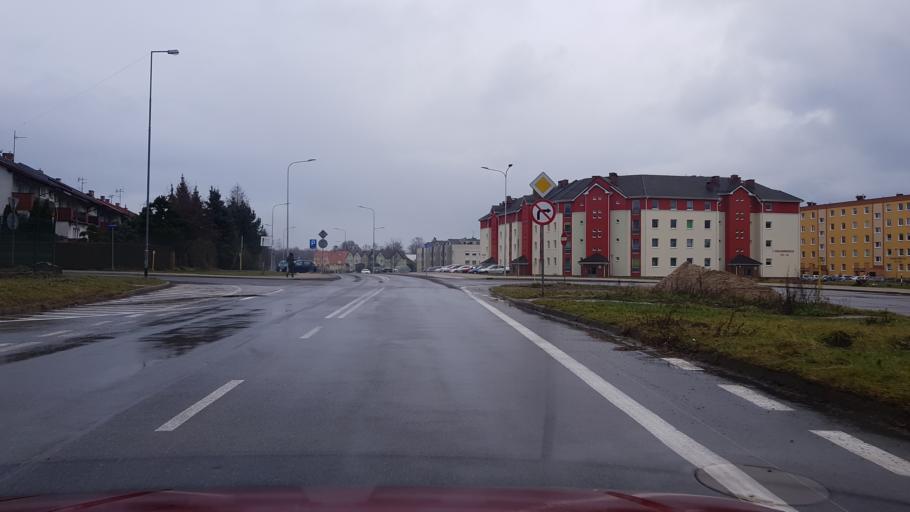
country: PL
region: West Pomeranian Voivodeship
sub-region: Koszalin
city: Koszalin
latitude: 54.1941
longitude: 16.2191
